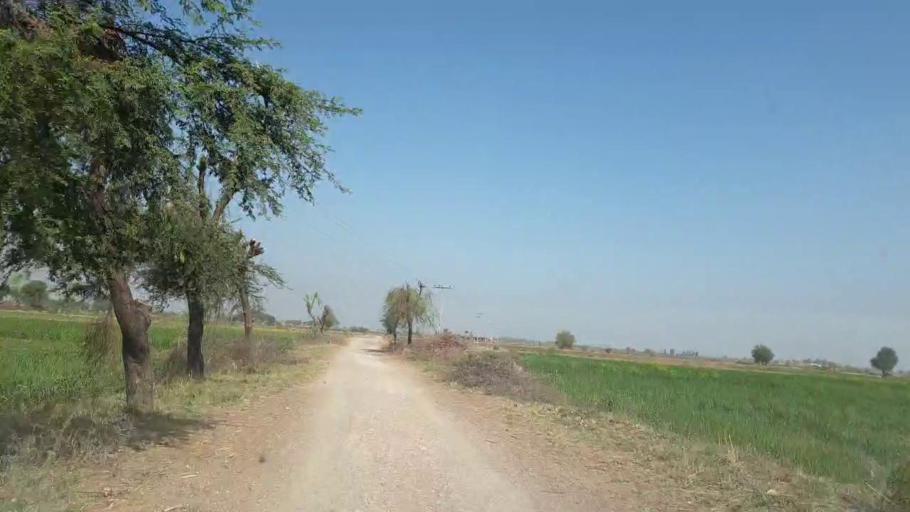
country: PK
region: Sindh
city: Mirpur Khas
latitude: 25.5640
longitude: 69.1836
